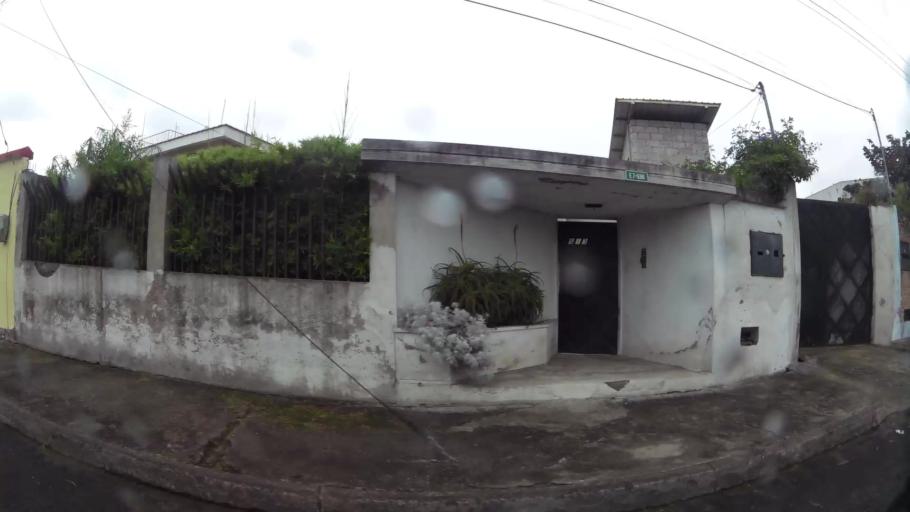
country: EC
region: Pichincha
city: Sangolqui
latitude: -0.2872
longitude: -78.4650
